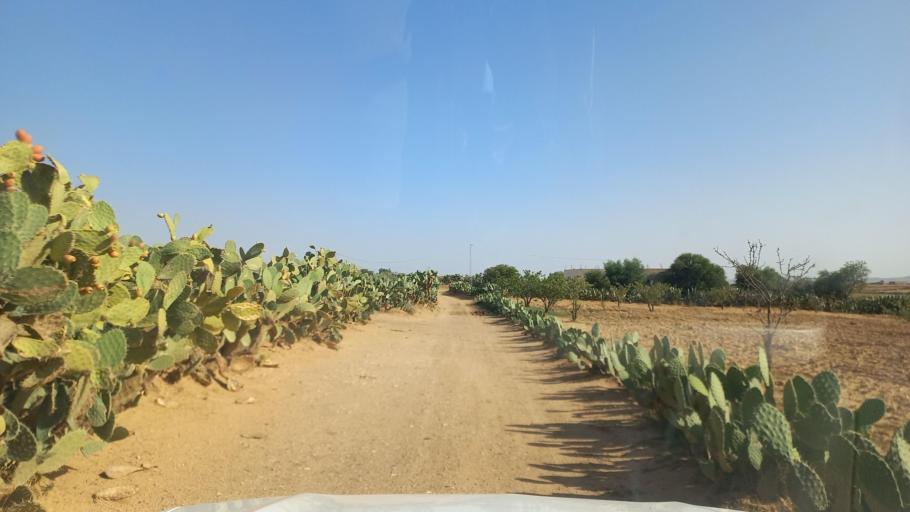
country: TN
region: Al Qasrayn
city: Sbiba
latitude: 35.3205
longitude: 9.0209
